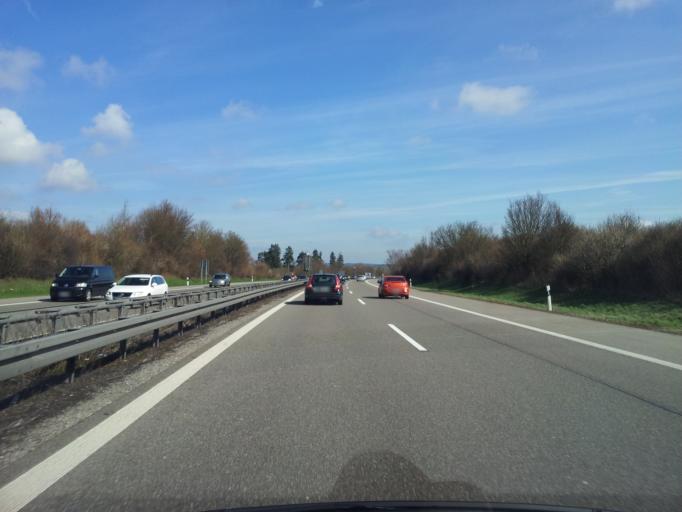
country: DE
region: Baden-Wuerttemberg
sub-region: Freiburg Region
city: Vohringen
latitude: 48.3356
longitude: 8.6476
